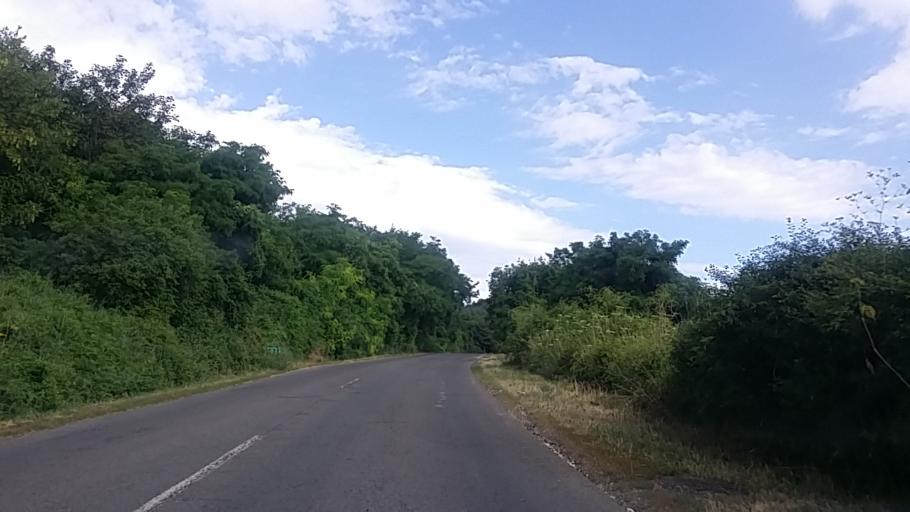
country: HU
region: Pest
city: Kosd
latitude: 47.8196
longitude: 19.2347
